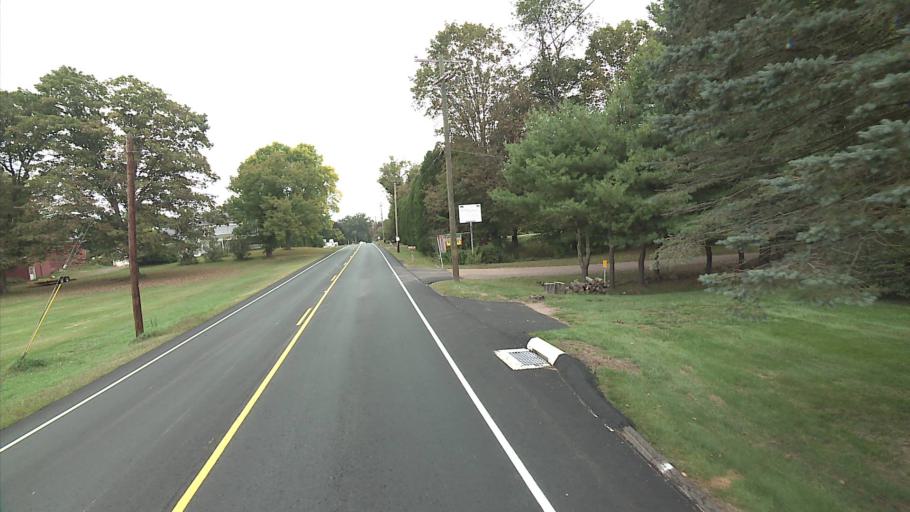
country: US
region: Connecticut
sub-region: Hartford County
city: Suffield Depot
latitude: 42.0291
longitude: -72.6888
